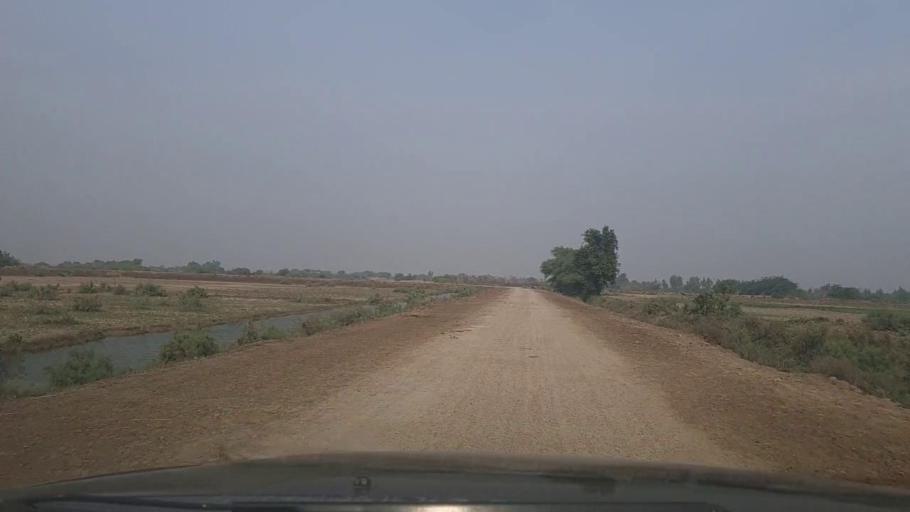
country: PK
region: Sindh
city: Mirpur Sakro
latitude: 24.5306
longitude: 67.7894
